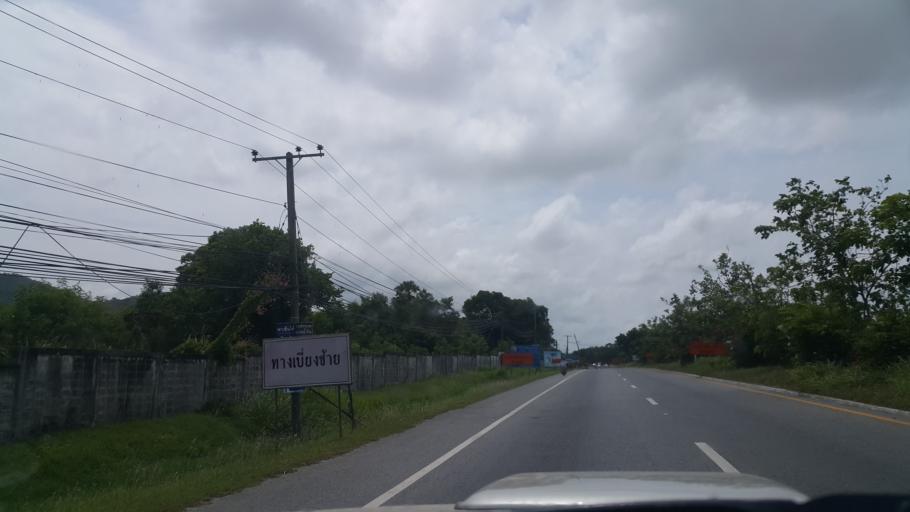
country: TH
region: Rayong
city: Ban Chang
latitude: 12.7075
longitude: 101.0218
